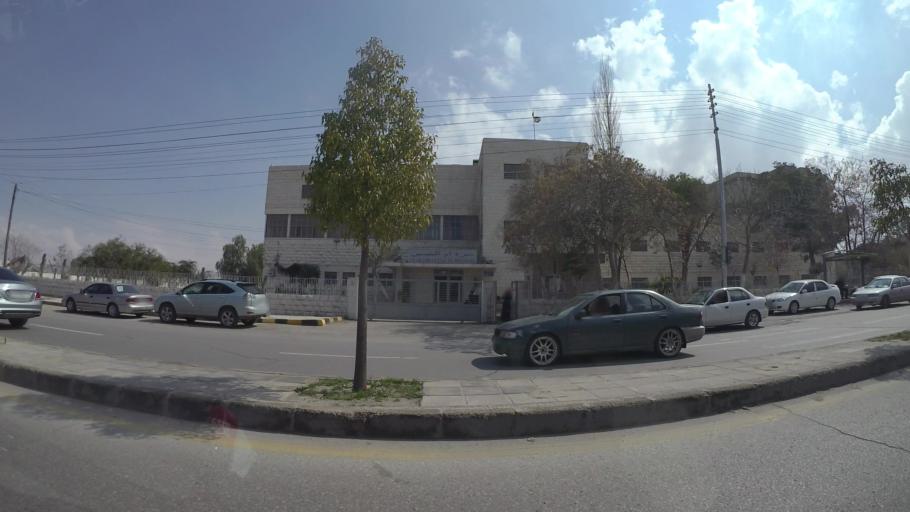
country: JO
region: Zarqa
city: Russeifa
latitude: 31.9858
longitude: 35.9974
